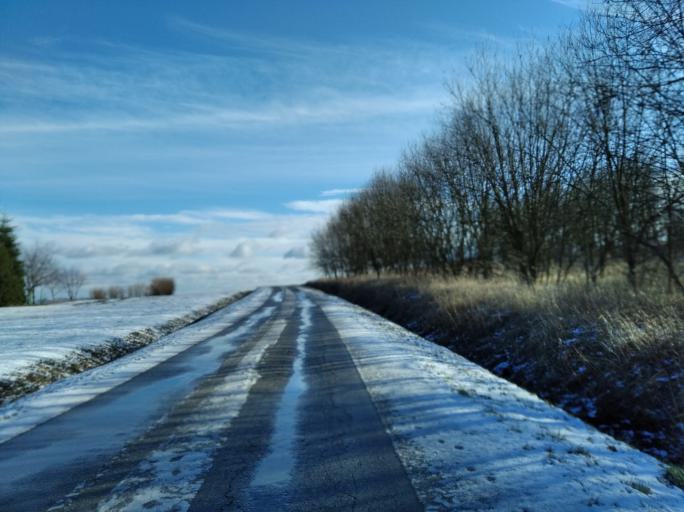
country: PL
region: Subcarpathian Voivodeship
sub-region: Powiat ropczycko-sedziszowski
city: Wielopole Skrzynskie
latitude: 49.9109
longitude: 21.6402
